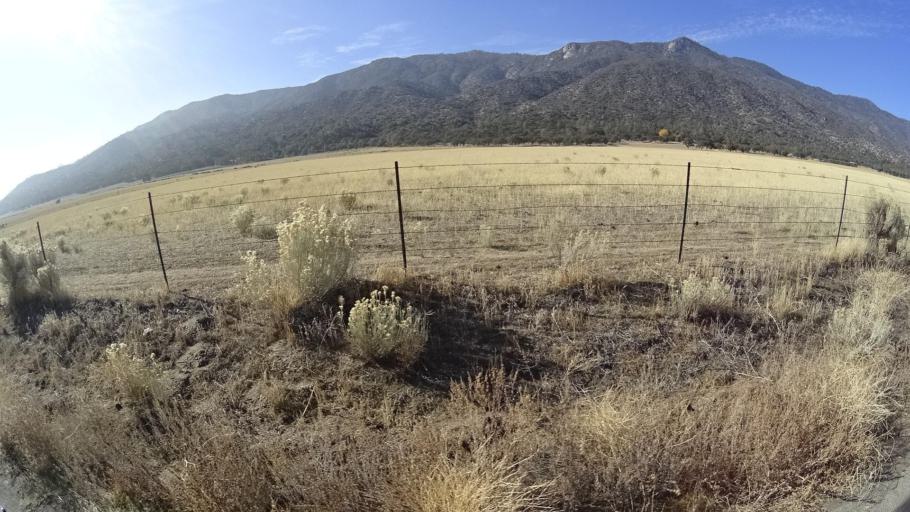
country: US
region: California
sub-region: Kern County
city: Bodfish
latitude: 35.4181
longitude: -118.5363
